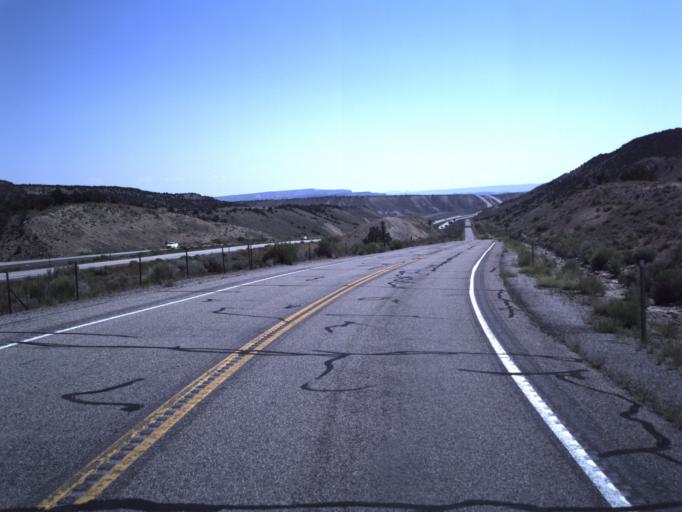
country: US
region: Utah
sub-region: Emery County
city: Ferron
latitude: 38.7562
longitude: -111.3800
